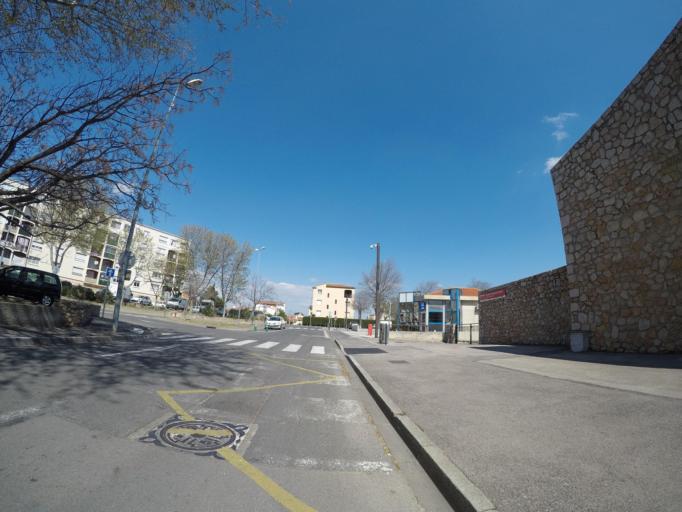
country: FR
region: Languedoc-Roussillon
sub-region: Departement des Pyrenees-Orientales
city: Perpignan
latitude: 42.6938
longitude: 2.9100
